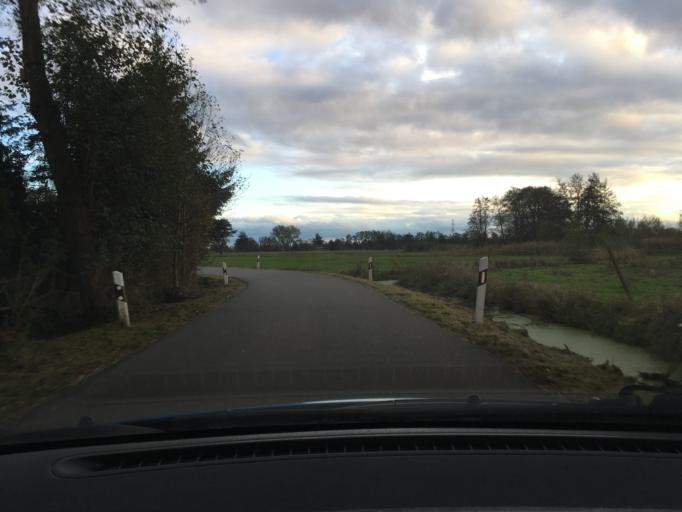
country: DE
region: Hamburg
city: Harburg
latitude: 53.4564
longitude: 10.0416
